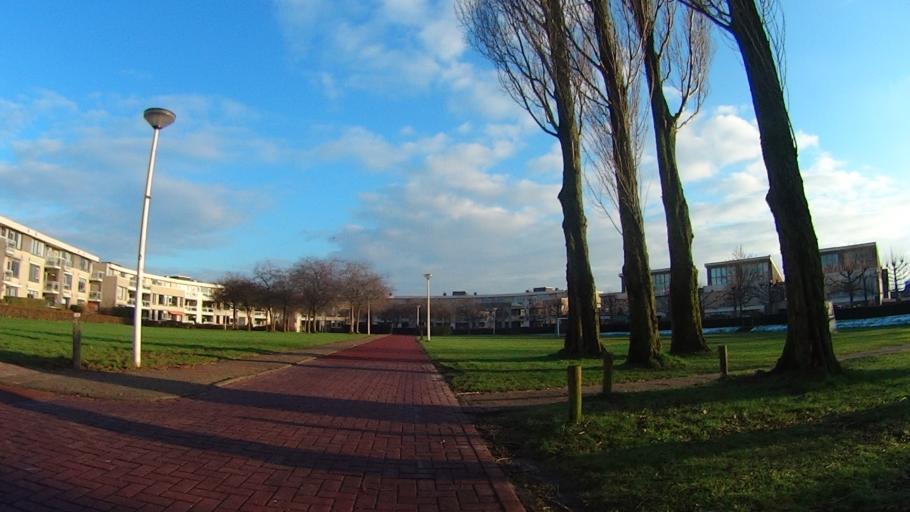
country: NL
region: Utrecht
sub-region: Gemeente Amersfoort
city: Hoogland
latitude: 52.1828
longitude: 5.3958
